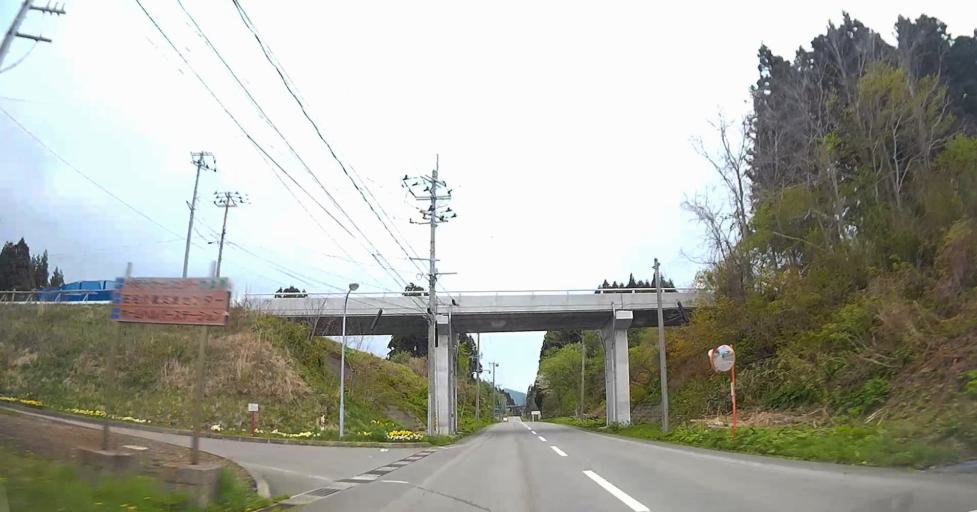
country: JP
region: Aomori
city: Goshogawara
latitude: 41.1777
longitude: 140.4798
